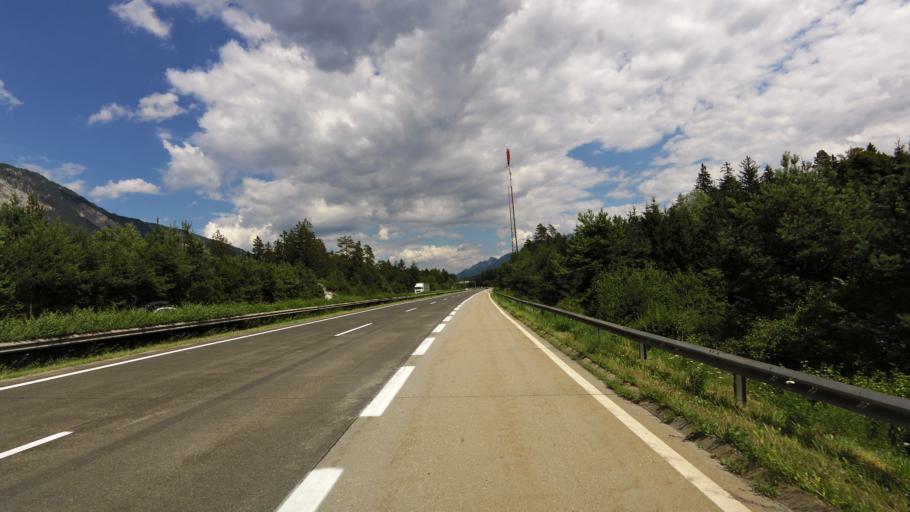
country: AT
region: Carinthia
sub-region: Politischer Bezirk Villach Land
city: Arnoldstein
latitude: 46.5701
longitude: 13.7041
